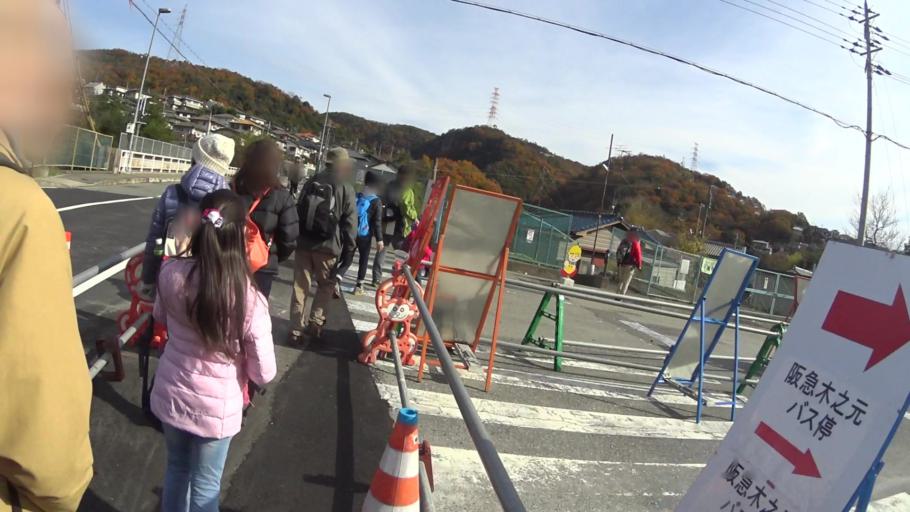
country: JP
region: Hyogo
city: Takarazuka
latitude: 34.8249
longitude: 135.3197
